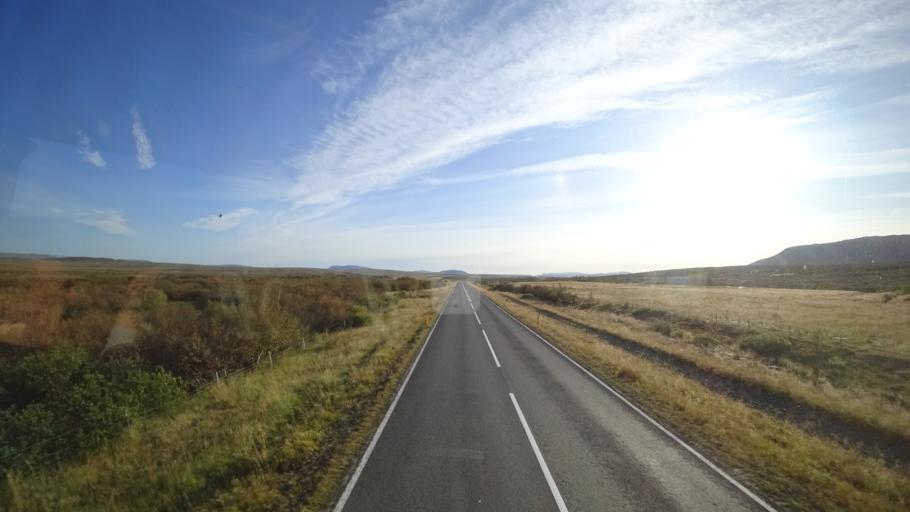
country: IS
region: South
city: Selfoss
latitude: 64.2627
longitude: -20.4700
